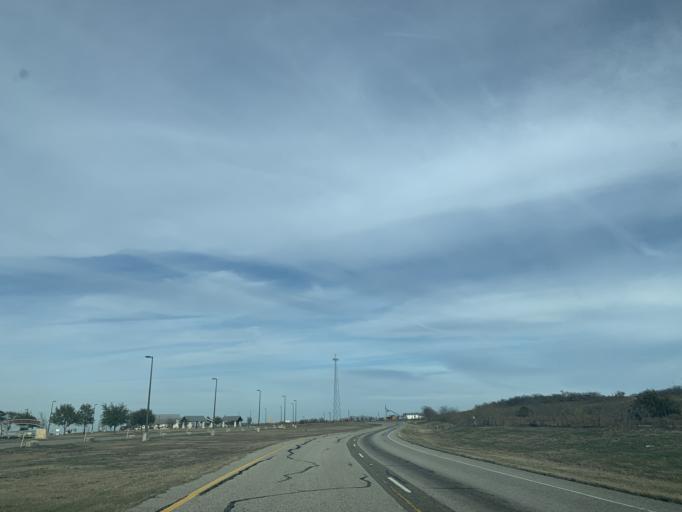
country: US
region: Texas
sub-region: Bell County
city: Salado
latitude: 30.8993
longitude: -97.5622
